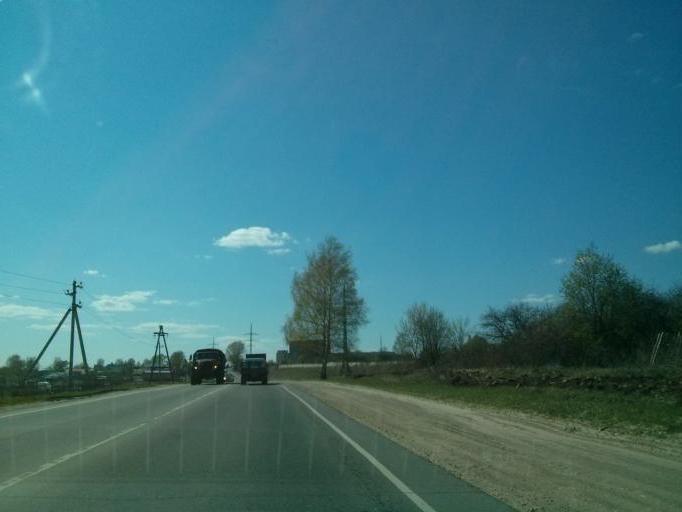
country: RU
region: Nizjnij Novgorod
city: Taremskoye
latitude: 55.9357
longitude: 43.0681
